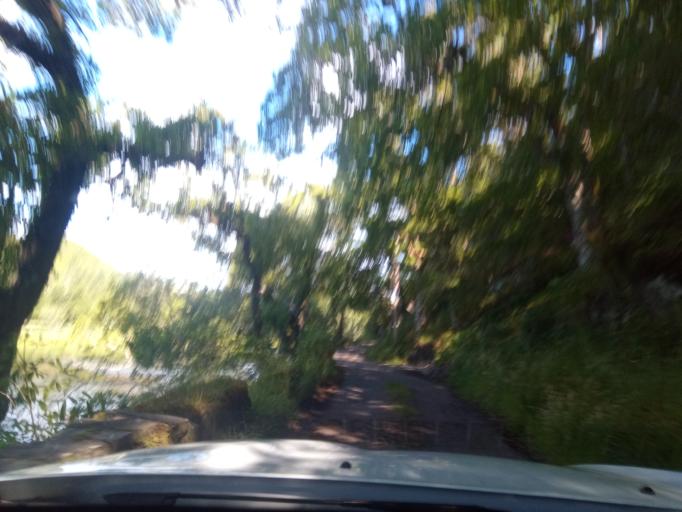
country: GB
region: Scotland
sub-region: Argyll and Bute
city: Isle Of Mull
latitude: 56.7615
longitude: -5.8184
